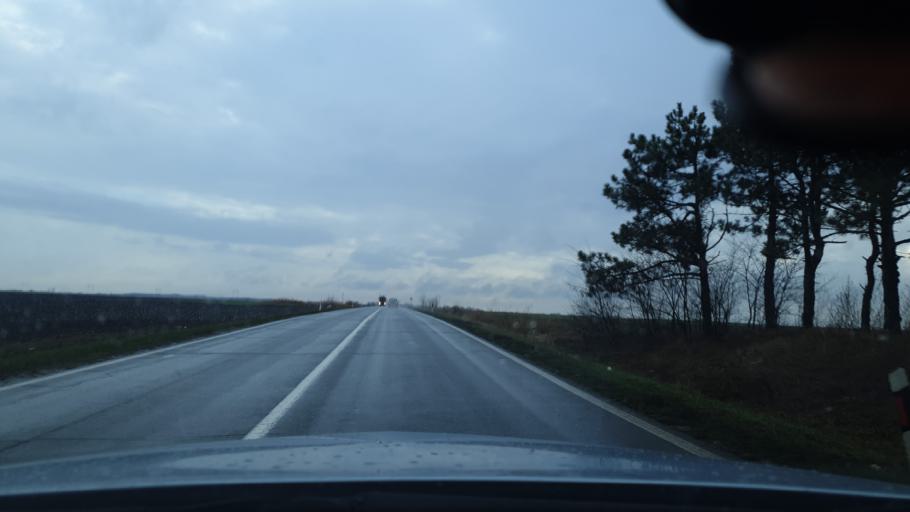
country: RS
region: Autonomna Pokrajina Vojvodina
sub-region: Juznobanatski Okrug
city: Kovin
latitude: 44.8308
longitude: 20.8319
